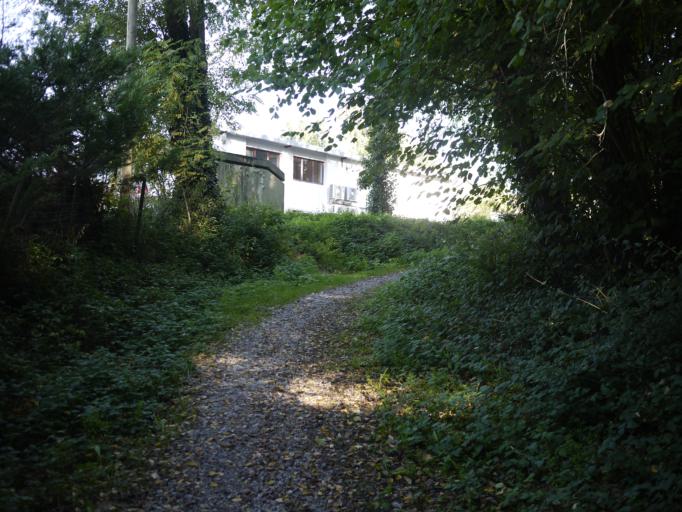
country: FR
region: Aquitaine
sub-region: Departement des Landes
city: Saint-Paul-les-Dax
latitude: 43.7241
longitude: -1.0672
